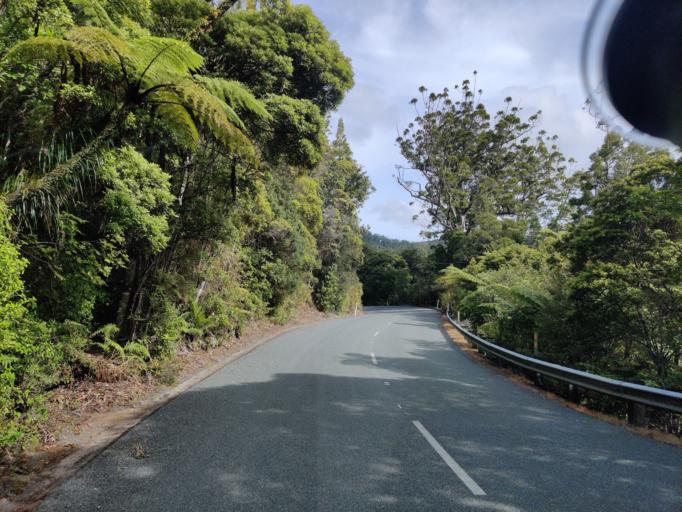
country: NZ
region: Northland
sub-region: Kaipara District
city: Dargaville
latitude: -35.6488
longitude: 173.5604
